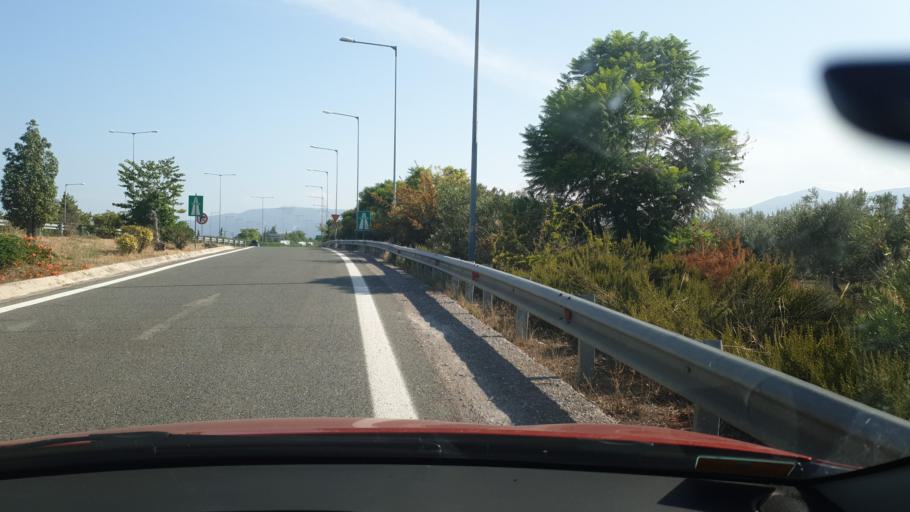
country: GR
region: Central Greece
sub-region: Nomos Fthiotidos
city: Livanates
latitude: 38.7059
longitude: 23.0556
